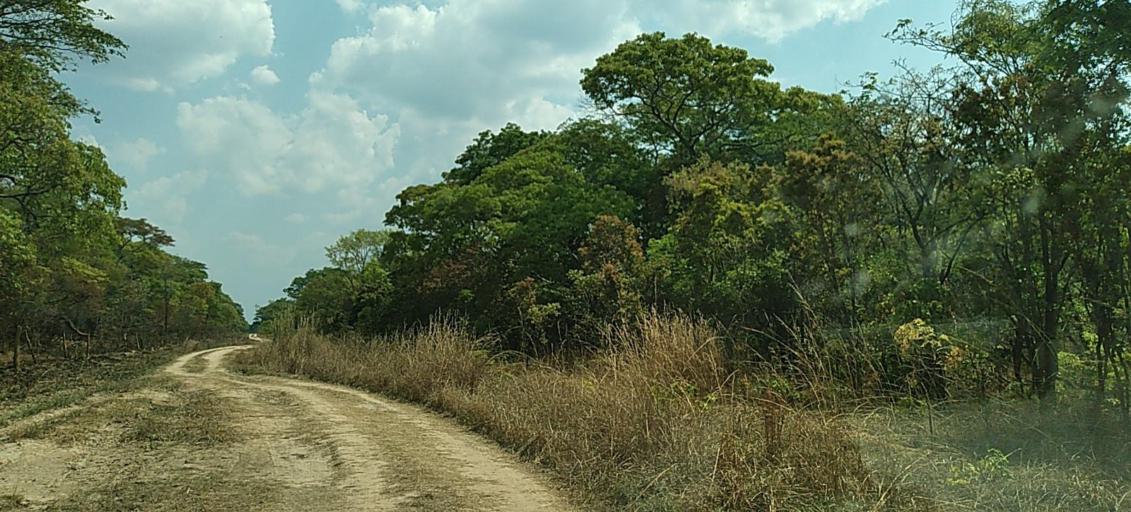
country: ZM
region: Copperbelt
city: Mpongwe
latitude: -13.8390
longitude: 27.9365
